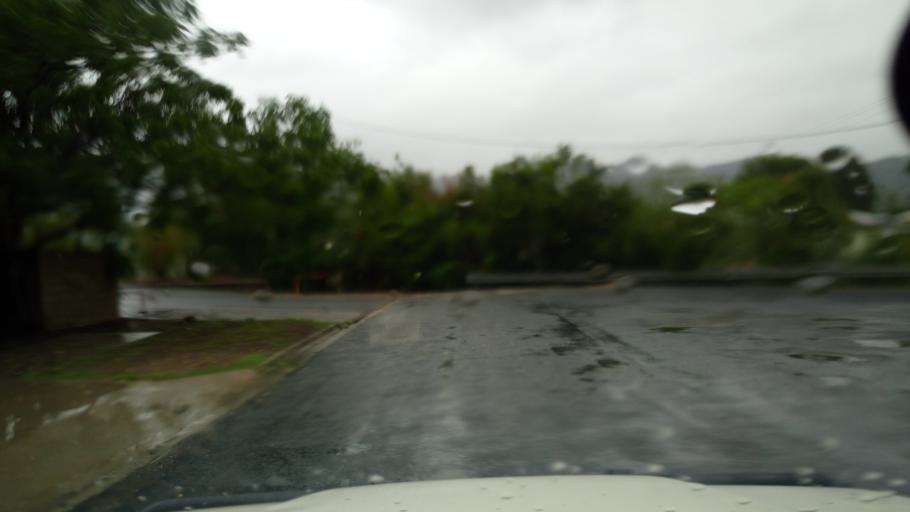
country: AU
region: Queensland
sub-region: Cairns
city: Woree
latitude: -16.9399
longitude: 145.7504
